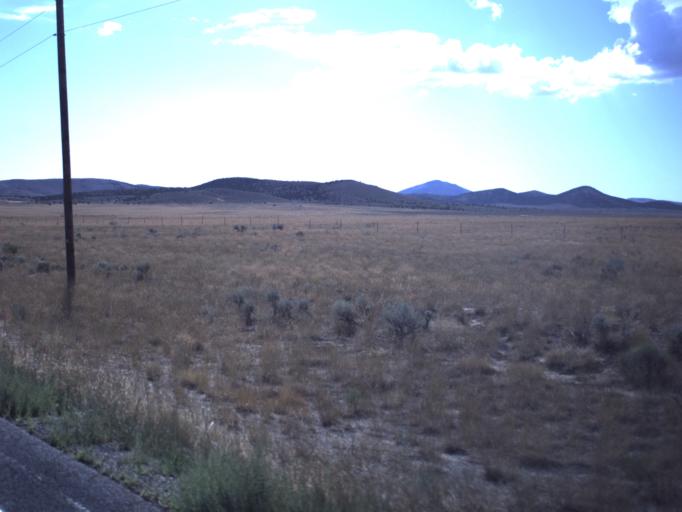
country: US
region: Utah
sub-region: Tooele County
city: Tooele
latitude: 40.0846
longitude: -112.4198
